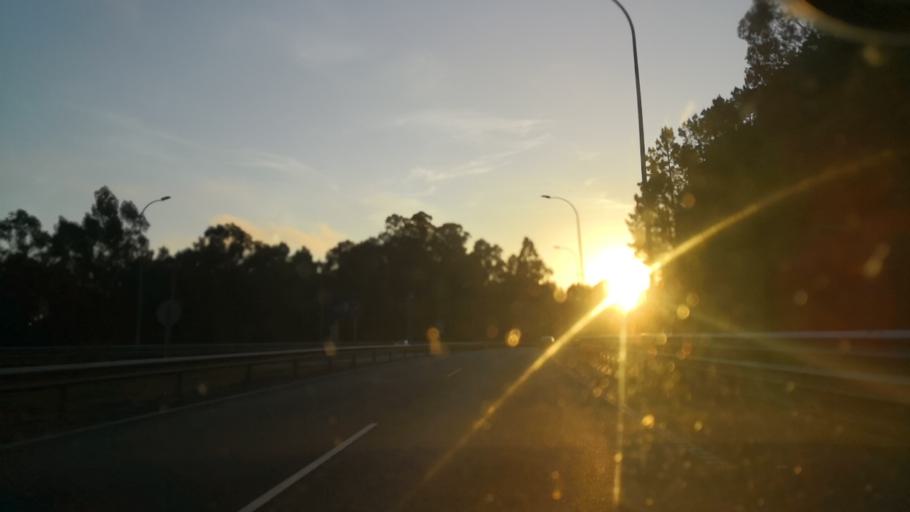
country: ES
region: Galicia
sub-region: Provincia de Pontevedra
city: Vigo
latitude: 42.2407
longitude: -8.6674
